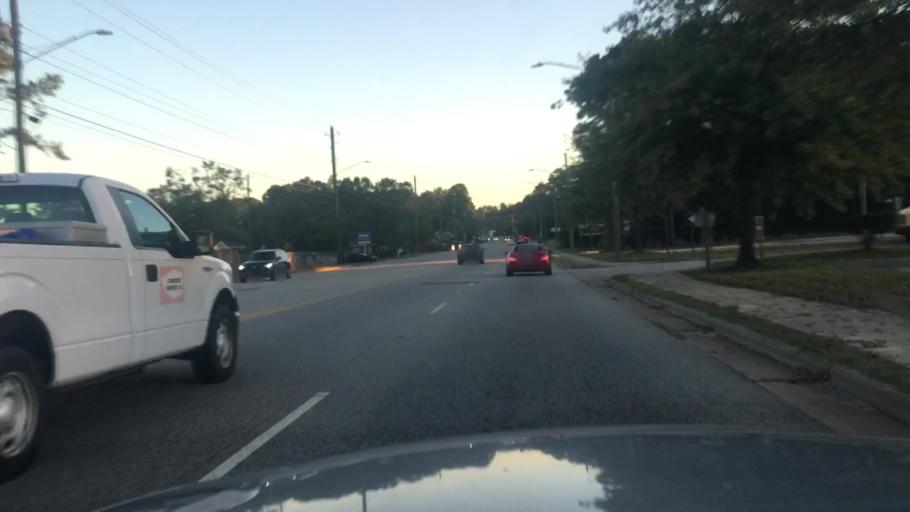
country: US
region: North Carolina
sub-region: Cumberland County
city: Hope Mills
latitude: 35.0183
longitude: -78.9633
